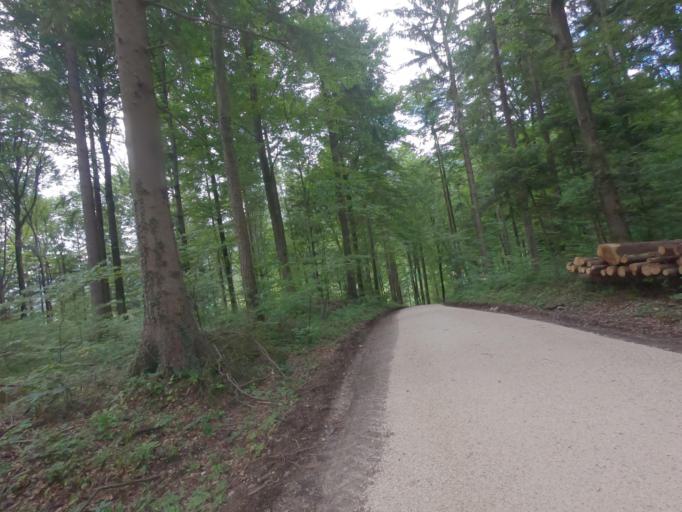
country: CH
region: Solothurn
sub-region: Bezirk Solothurn
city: Solothurn
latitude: 47.2347
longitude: 7.5410
